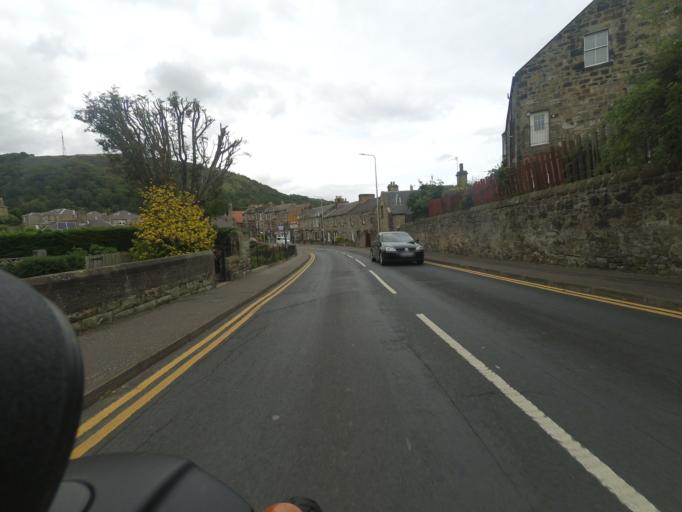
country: GB
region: Scotland
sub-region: Fife
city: Burntisland
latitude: 56.0624
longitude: -3.2289
